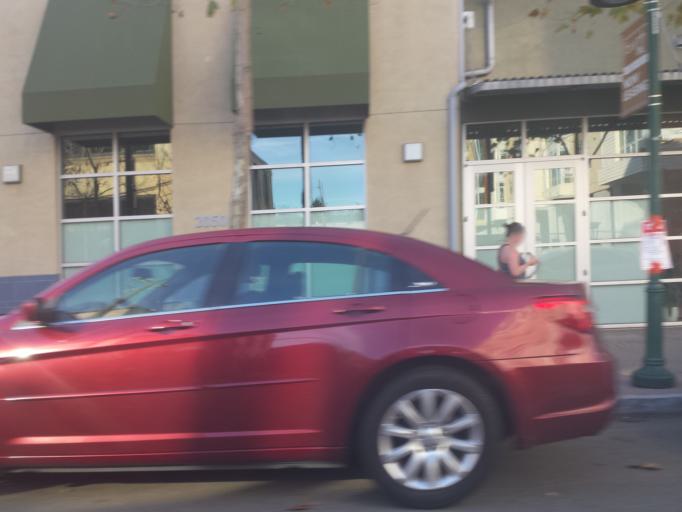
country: US
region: California
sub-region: Alameda County
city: Albany
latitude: 37.8667
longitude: -122.2997
